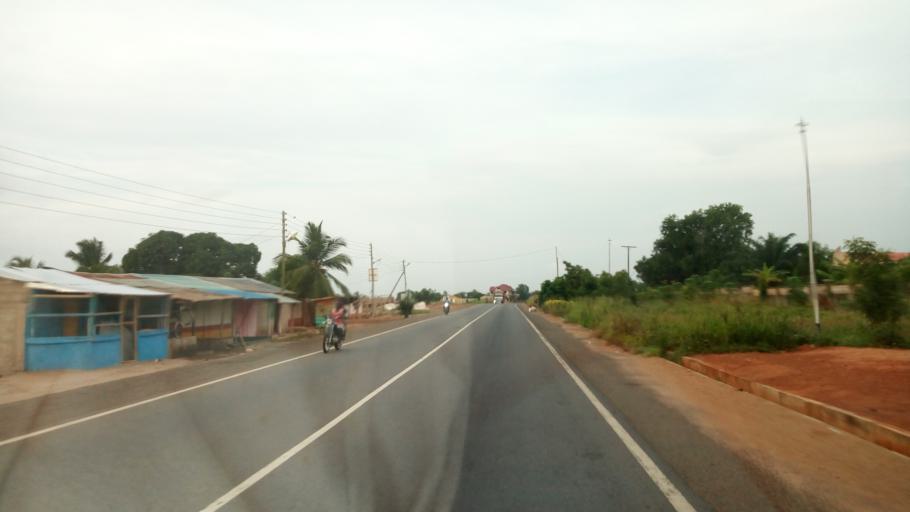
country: TG
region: Maritime
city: Lome
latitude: 6.1153
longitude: 1.1299
